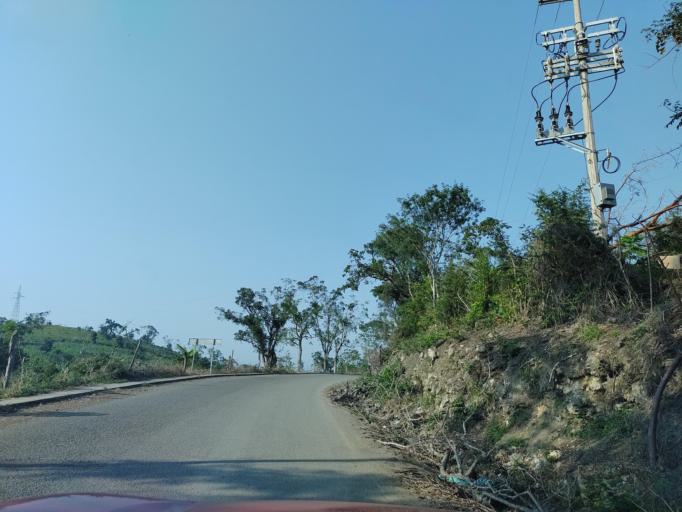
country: MX
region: Veracruz
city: Agua Dulce
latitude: 20.3709
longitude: -97.1841
